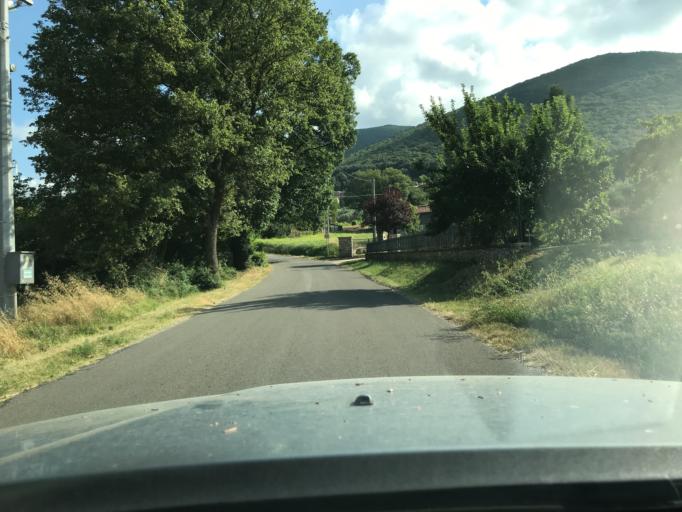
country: IT
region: Umbria
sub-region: Provincia di Terni
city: Guardea
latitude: 42.6280
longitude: 12.3170
